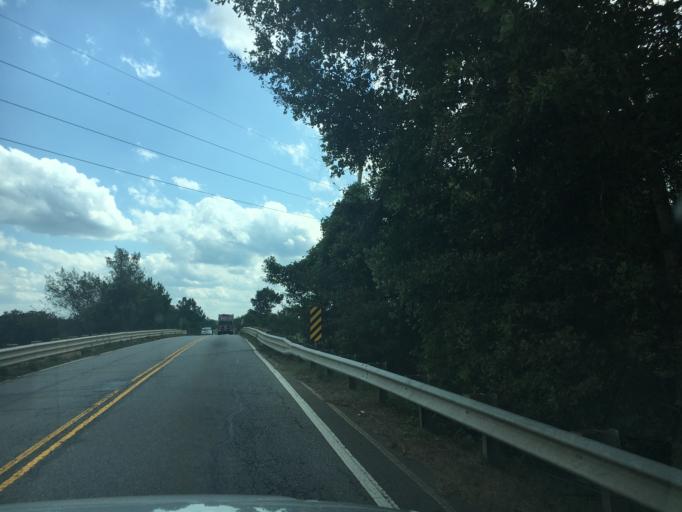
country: US
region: South Carolina
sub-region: Anderson County
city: Williamston
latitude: 34.5988
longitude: -82.4986
